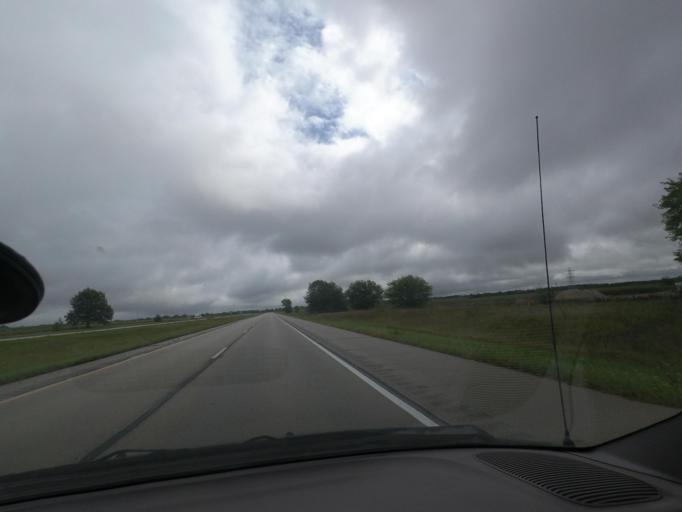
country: US
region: Illinois
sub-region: Piatt County
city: Monticello
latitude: 40.0308
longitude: -88.6157
